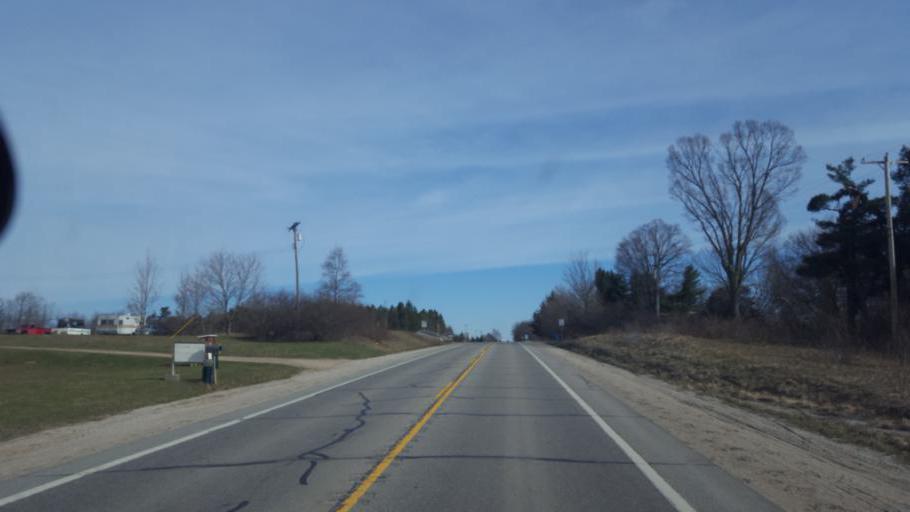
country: US
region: Michigan
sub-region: Montcalm County
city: Howard City
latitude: 43.5093
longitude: -85.4432
